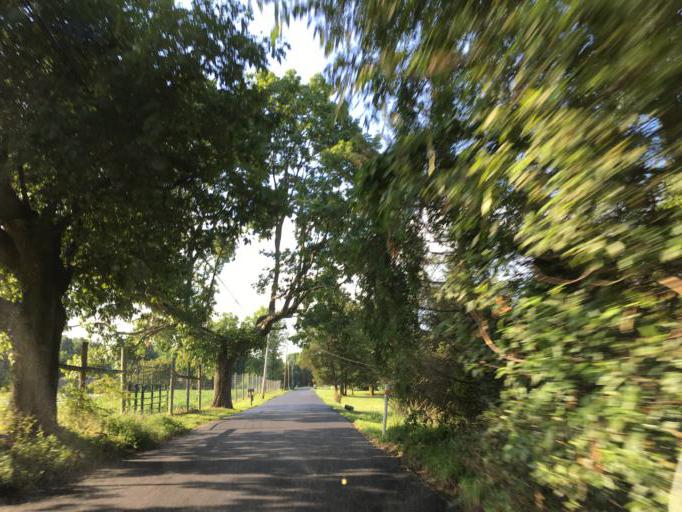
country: US
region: Maryland
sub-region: Baltimore County
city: Kingsville
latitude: 39.4558
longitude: -76.4386
